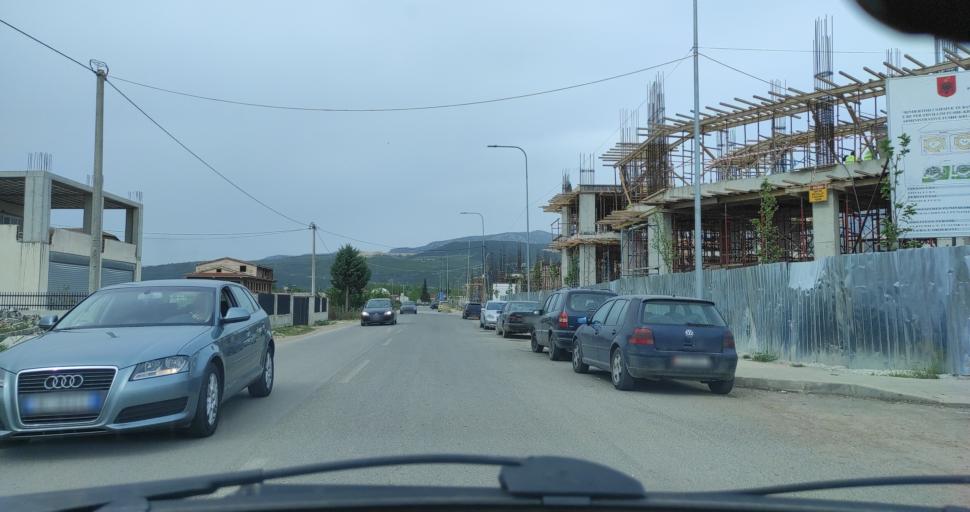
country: AL
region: Durres
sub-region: Rrethi i Krujes
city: Fushe-Kruje
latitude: 41.4849
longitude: 19.7249
